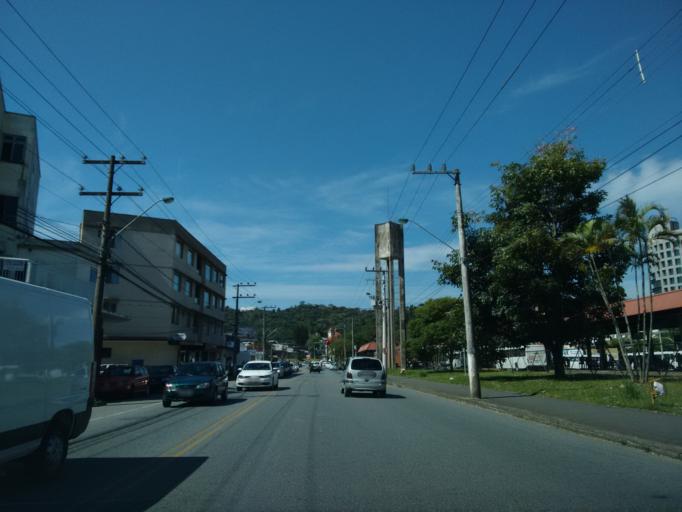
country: BR
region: Santa Catarina
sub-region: Blumenau
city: Blumenau
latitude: -26.9288
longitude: -49.0582
